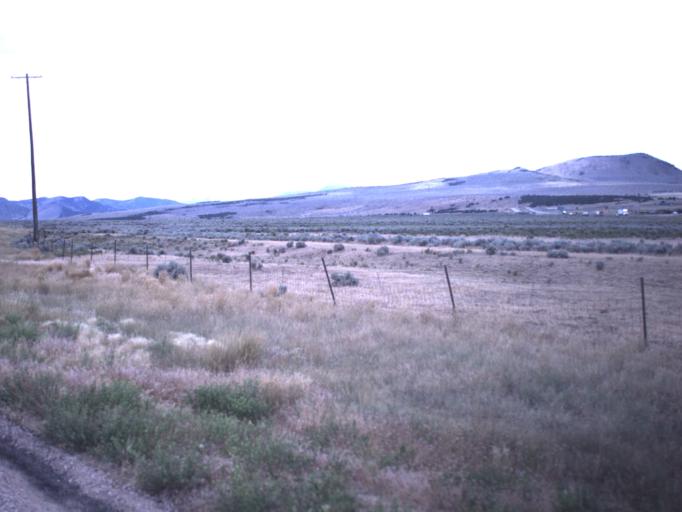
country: US
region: Utah
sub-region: Beaver County
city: Beaver
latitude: 38.5855
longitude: -112.5846
